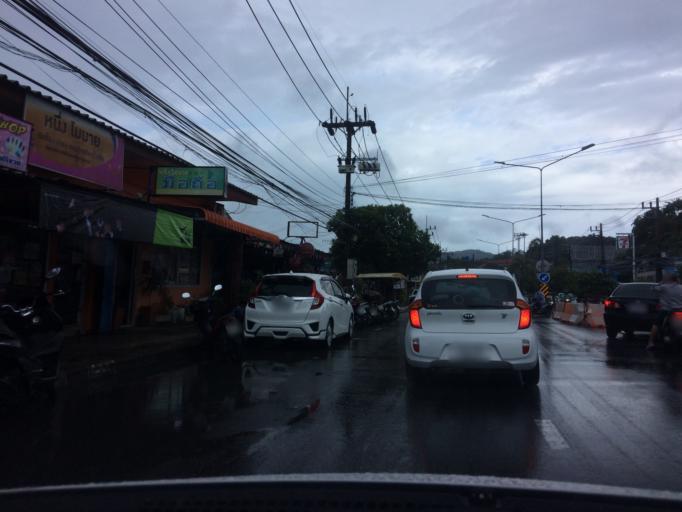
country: TH
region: Phuket
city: Kathu
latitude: 7.9123
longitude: 98.3332
